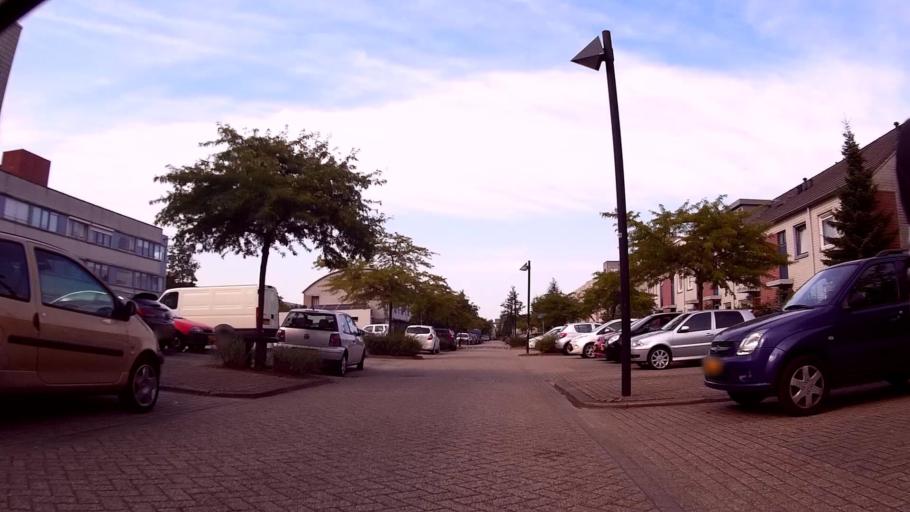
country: NL
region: Utrecht
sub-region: Gemeente Utrecht
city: Utrecht
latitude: 52.1093
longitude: 5.1461
